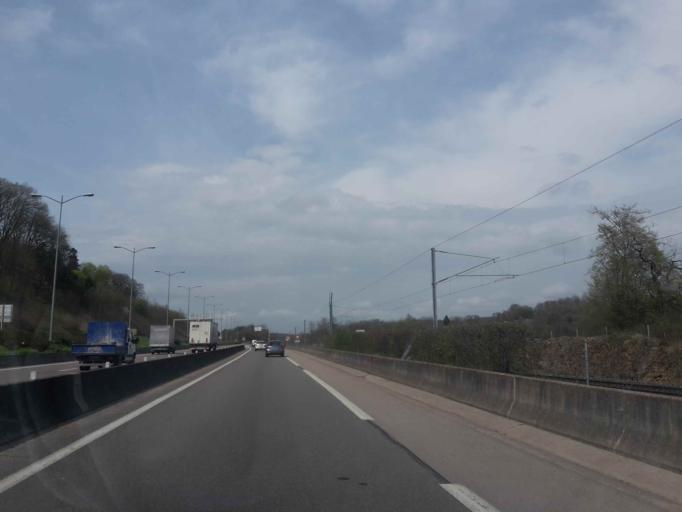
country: FR
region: Franche-Comte
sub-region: Departement du Doubs
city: Besancon
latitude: 47.2657
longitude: 6.0052
